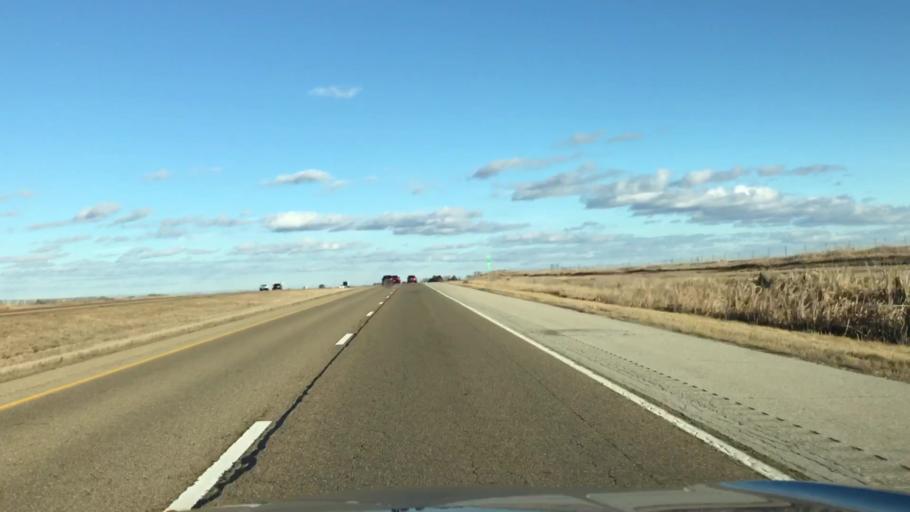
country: US
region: Illinois
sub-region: McLean County
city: Lexington
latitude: 40.6583
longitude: -88.7877
